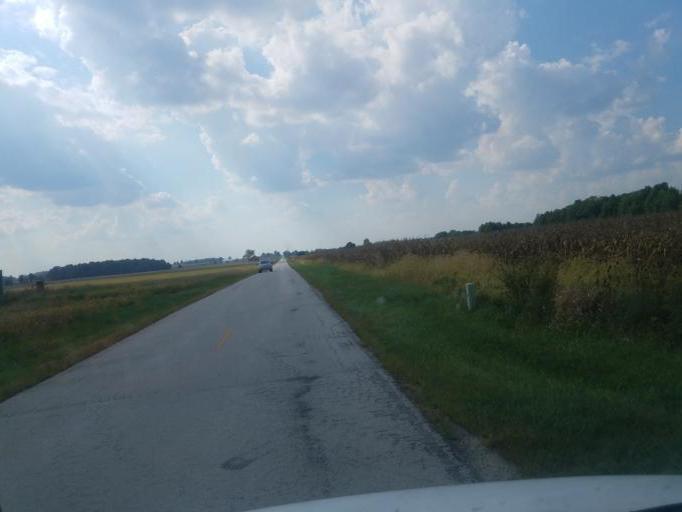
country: US
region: Ohio
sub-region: Hardin County
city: Kenton
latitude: 40.7462
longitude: -83.6238
